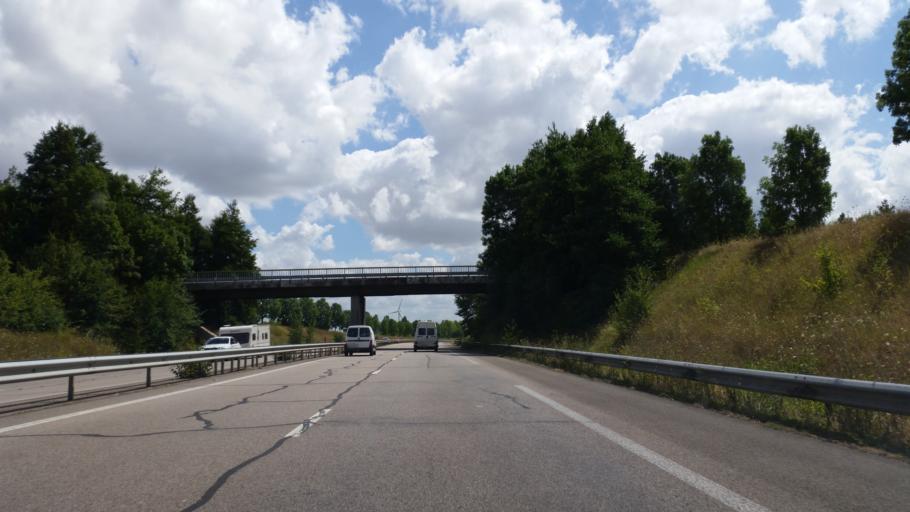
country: FR
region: Lower Normandy
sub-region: Departement du Calvados
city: Potigny
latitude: 48.9465
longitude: -0.2164
